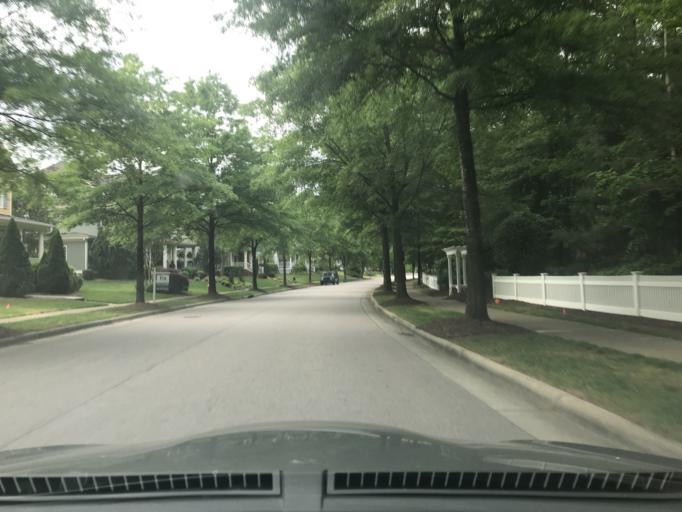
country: US
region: North Carolina
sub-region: Wake County
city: Wake Forest
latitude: 35.9259
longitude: -78.5597
